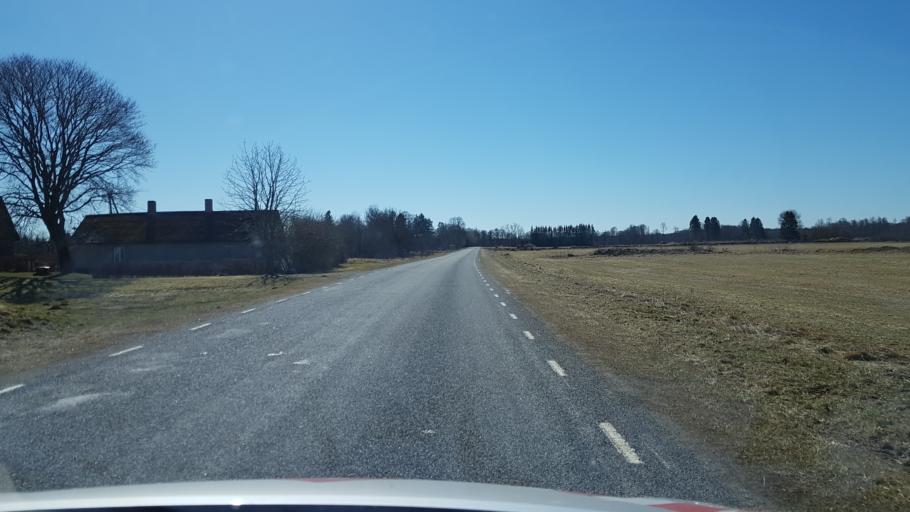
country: EE
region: Laeaene-Virumaa
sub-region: Haljala vald
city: Haljala
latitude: 59.5327
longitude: 26.2359
